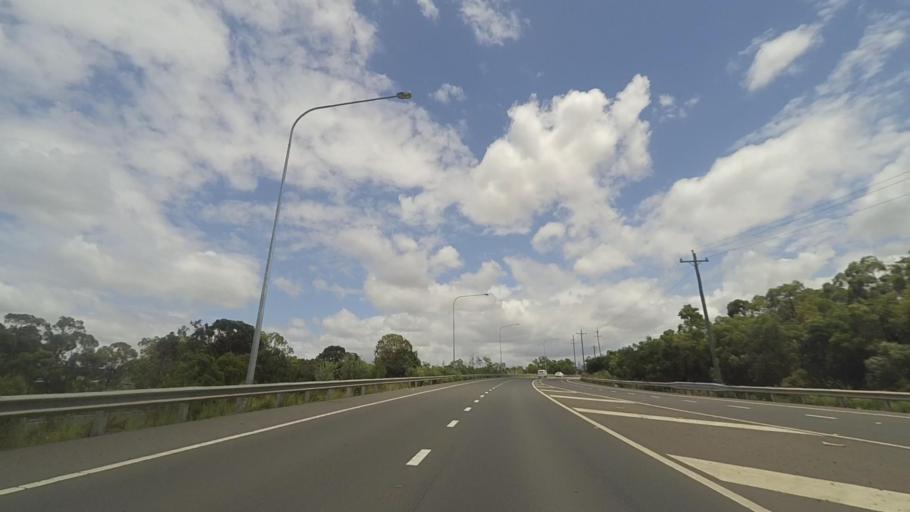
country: AU
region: New South Wales
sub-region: Liverpool
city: Holsworthy
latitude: -33.9643
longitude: 150.9634
